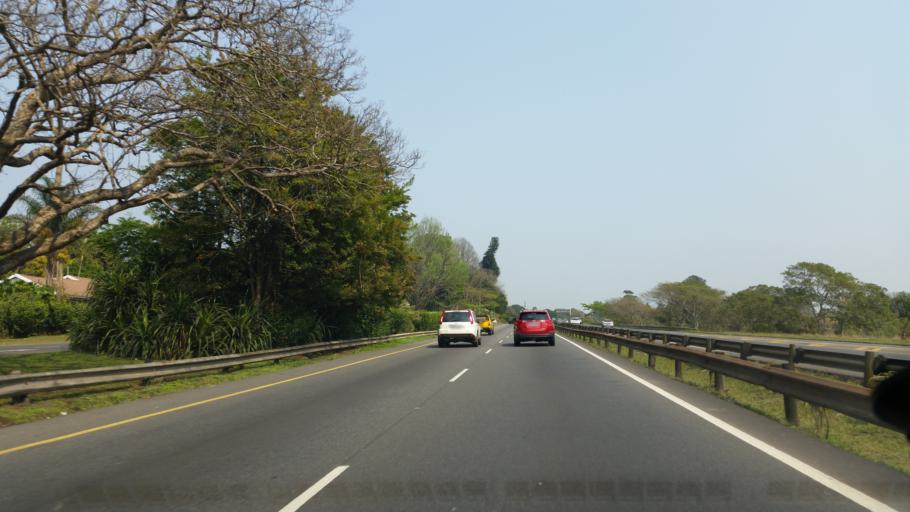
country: ZA
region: KwaZulu-Natal
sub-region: eThekwini Metropolitan Municipality
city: Mpumalanga
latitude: -29.7931
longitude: 30.8192
